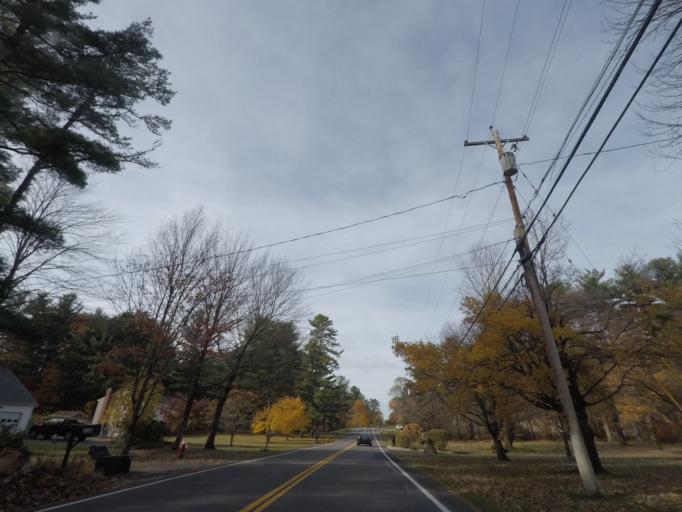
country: US
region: New York
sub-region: Schenectady County
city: Rotterdam
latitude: 42.7487
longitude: -73.9333
